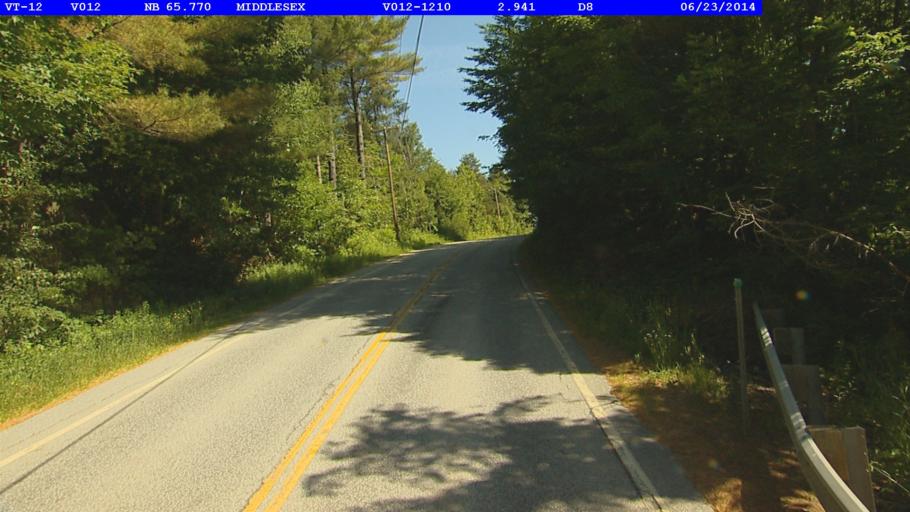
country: US
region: Vermont
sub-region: Washington County
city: Montpelier
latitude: 44.3427
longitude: -72.5660
